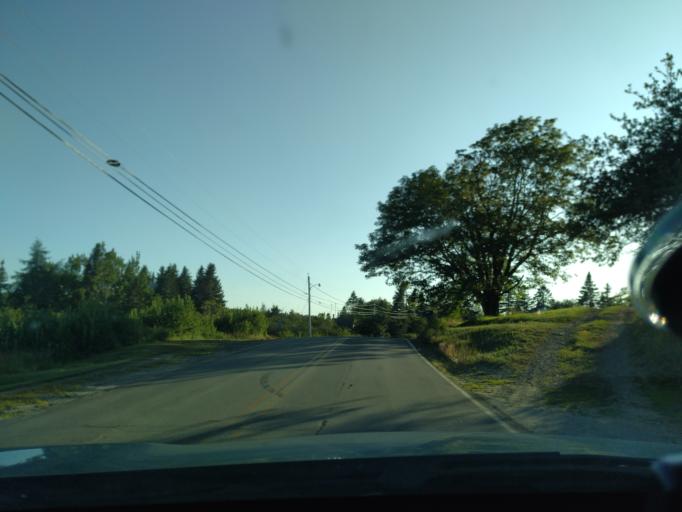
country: US
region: Maine
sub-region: Washington County
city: Machiasport
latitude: 44.6606
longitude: -67.2293
